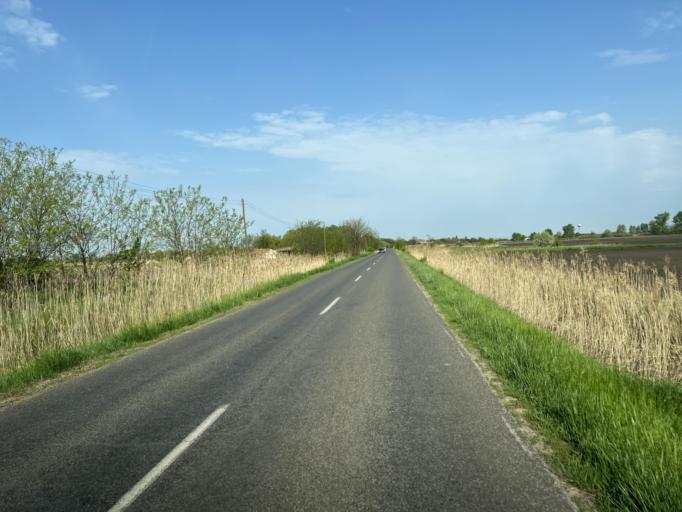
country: HU
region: Pest
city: Jaszkarajeno
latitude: 47.0471
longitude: 20.0841
